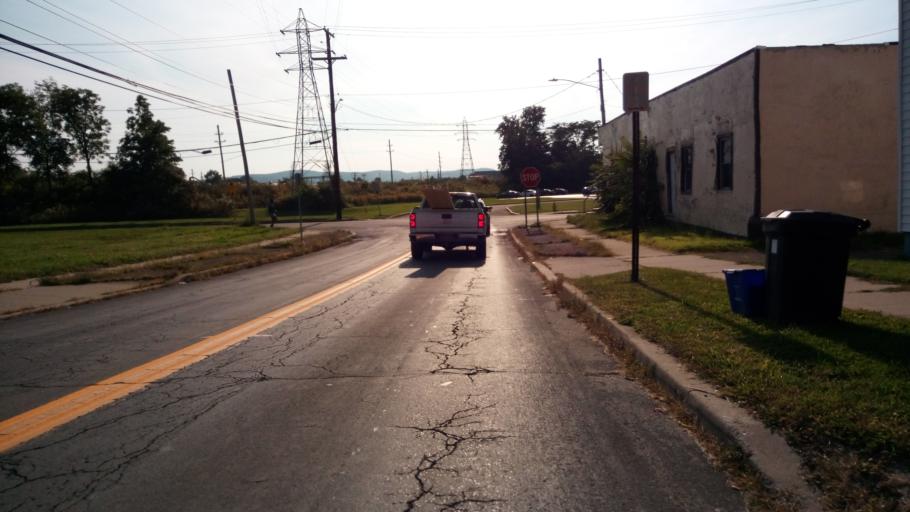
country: US
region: New York
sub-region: Chemung County
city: Elmira
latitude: 42.0990
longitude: -76.7960
